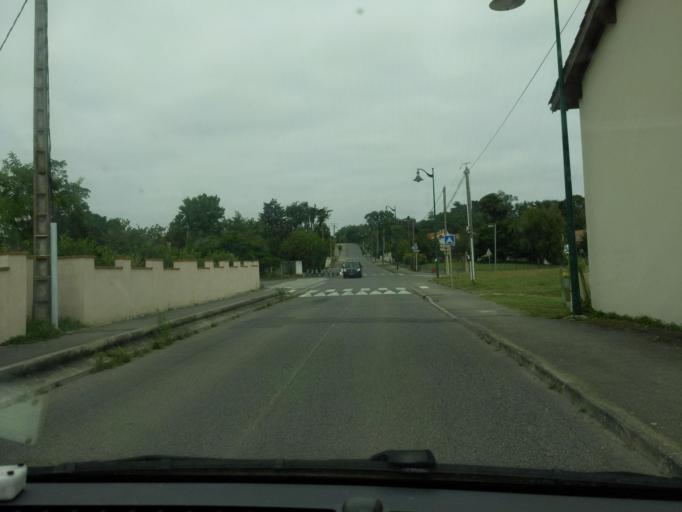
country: FR
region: Midi-Pyrenees
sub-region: Departement de la Haute-Garonne
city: Escalquens
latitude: 43.5224
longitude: 1.5620
